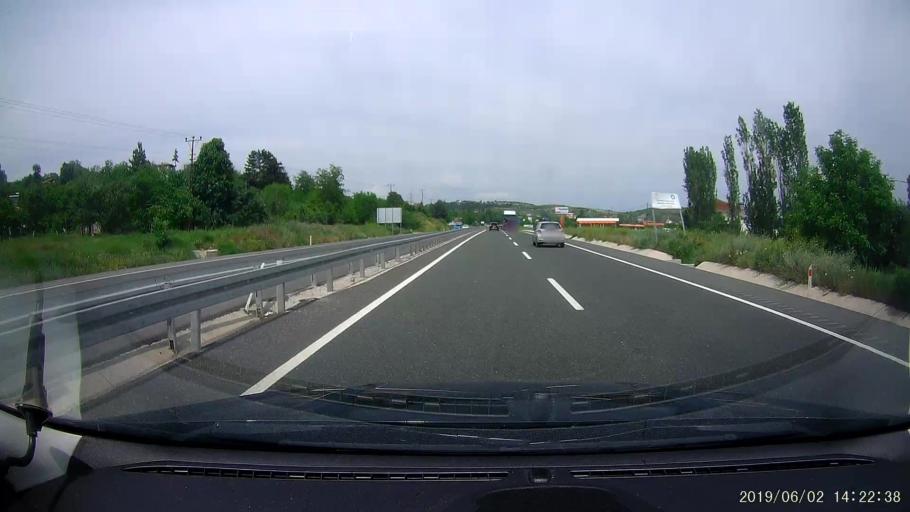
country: TR
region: Kastamonu
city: Tosya
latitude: 40.9970
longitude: 34.0199
